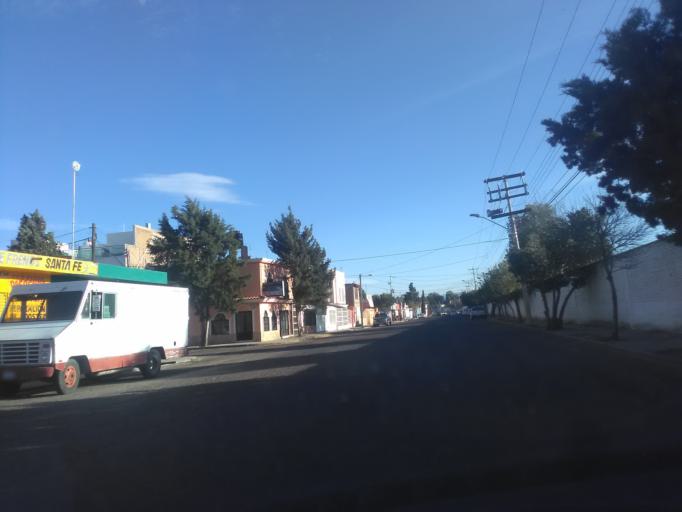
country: MX
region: Durango
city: Victoria de Durango
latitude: 24.0296
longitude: -104.6344
